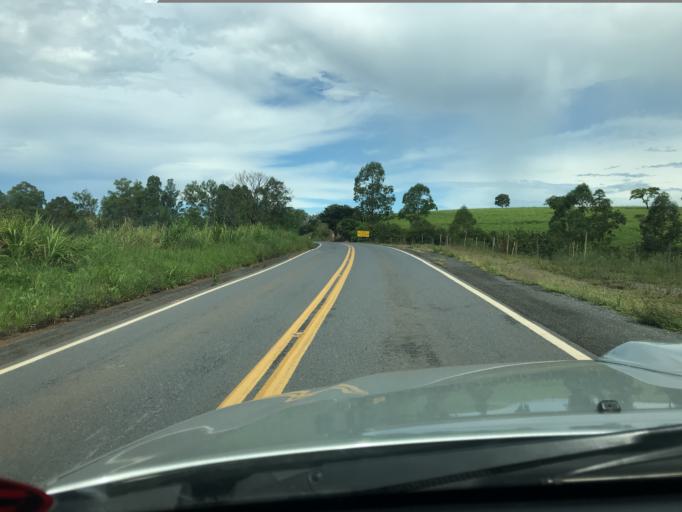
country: BR
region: Minas Gerais
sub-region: Bambui
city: Bambui
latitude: -19.8547
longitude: -45.9918
